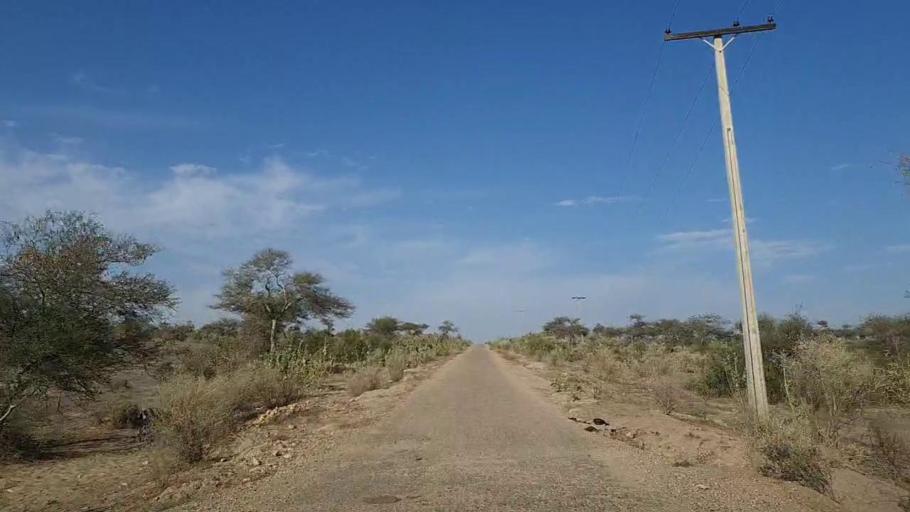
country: PK
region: Sindh
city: Naukot
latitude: 24.8560
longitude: 69.5235
